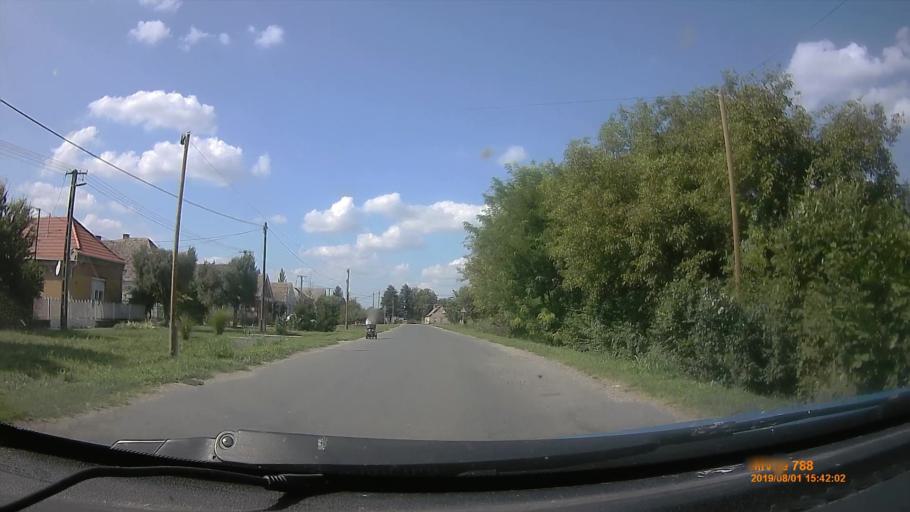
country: HU
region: Baranya
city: Szentlorinc
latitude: 45.9947
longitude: 17.9619
